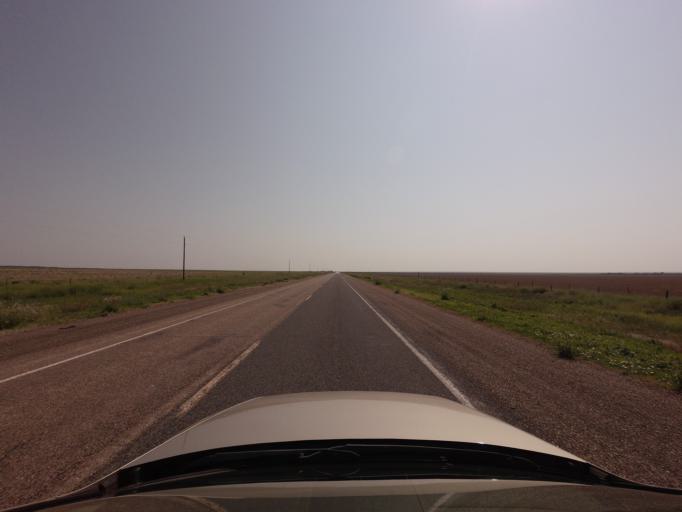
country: US
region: New Mexico
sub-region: Quay County
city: Tucumcari
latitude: 34.8234
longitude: -103.7328
